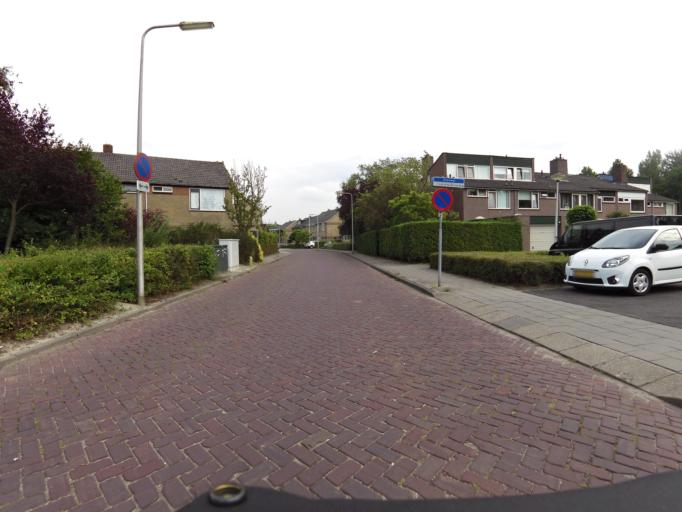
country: NL
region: South Holland
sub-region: Gemeente Maassluis
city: Maassluis
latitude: 51.8817
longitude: 4.2190
